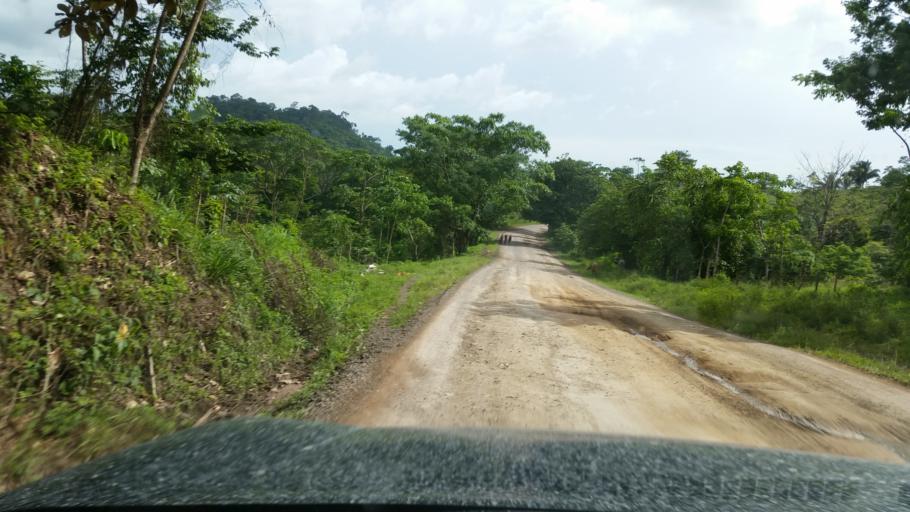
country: NI
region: Atlantico Norte (RAAN)
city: Siuna
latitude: 13.5955
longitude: -84.8055
